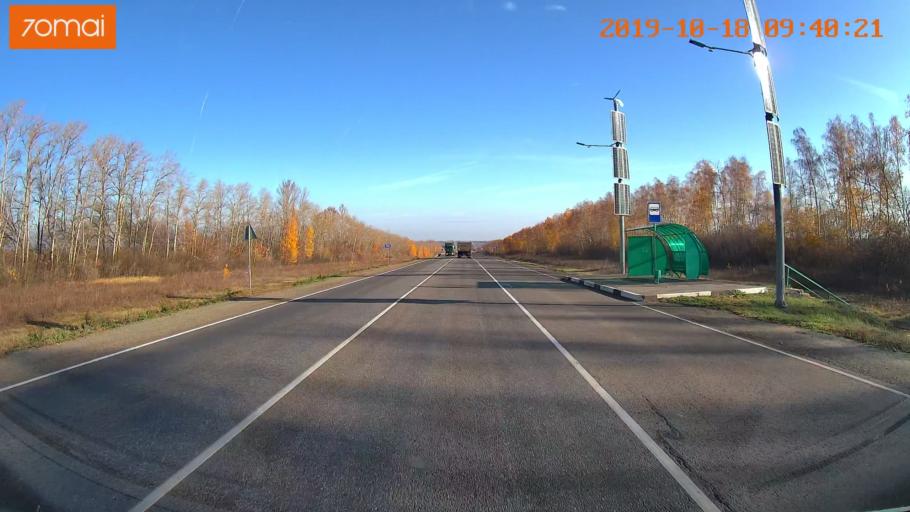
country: RU
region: Tula
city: Yefremov
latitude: 53.2630
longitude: 38.1469
